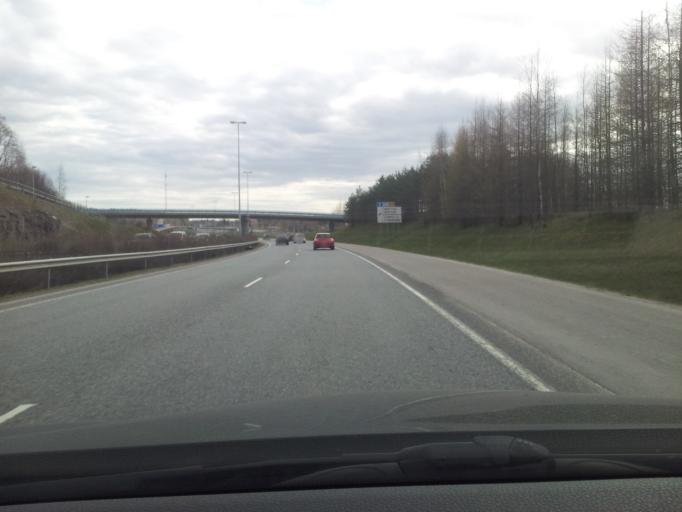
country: FI
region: Uusimaa
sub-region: Helsinki
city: Kauniainen
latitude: 60.1947
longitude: 24.7432
